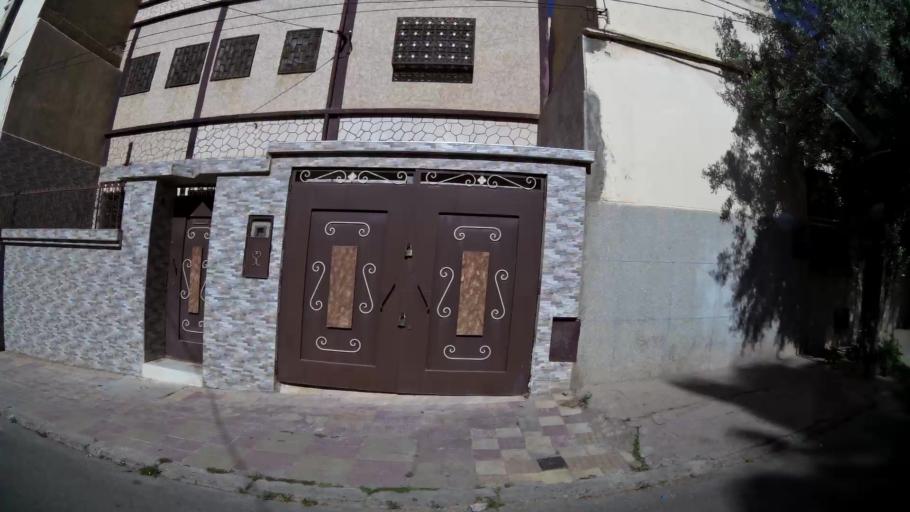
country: MA
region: Oriental
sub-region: Oujda-Angad
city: Oujda
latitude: 34.6721
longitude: -1.9138
